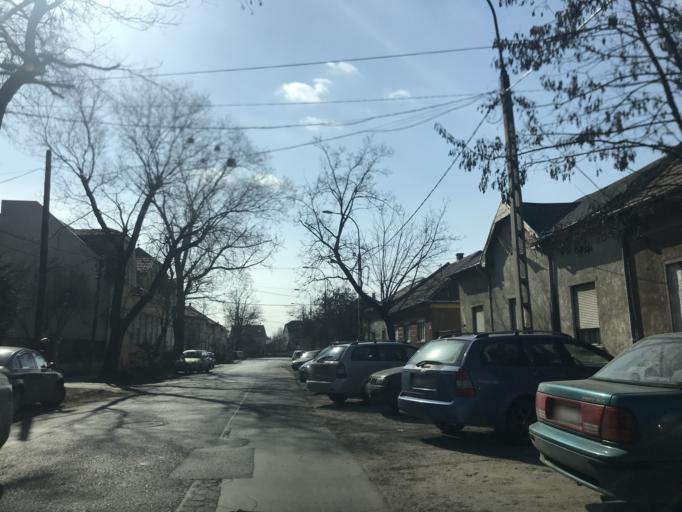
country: HU
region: Budapest
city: Budapest XIV. keruelet
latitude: 47.5363
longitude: 19.1170
